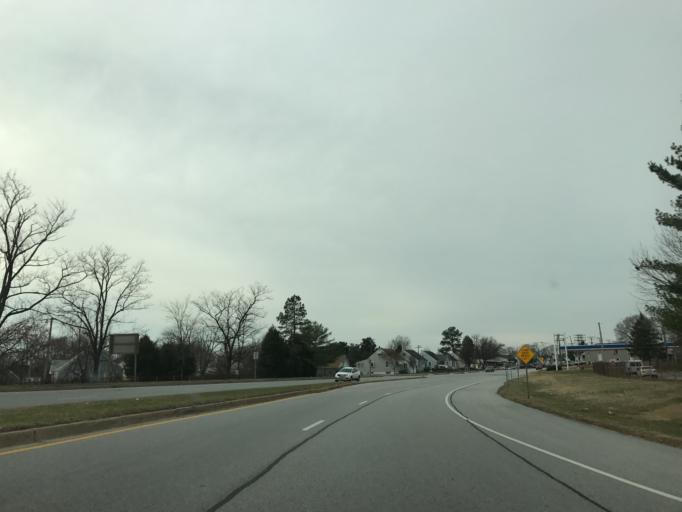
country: US
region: Maryland
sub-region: Anne Arundel County
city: Glen Burnie
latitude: 39.1571
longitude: -76.6063
